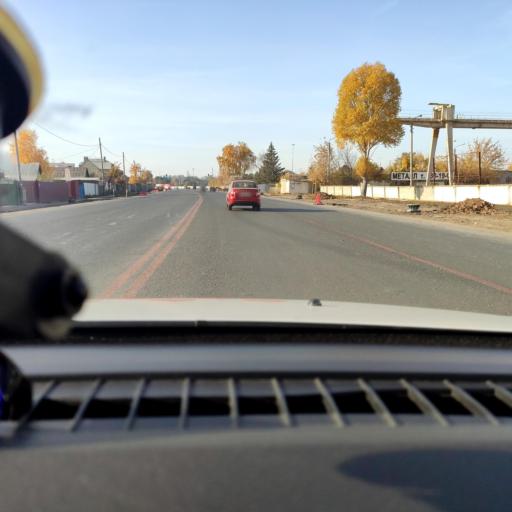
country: RU
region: Samara
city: Samara
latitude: 53.1315
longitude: 50.0953
